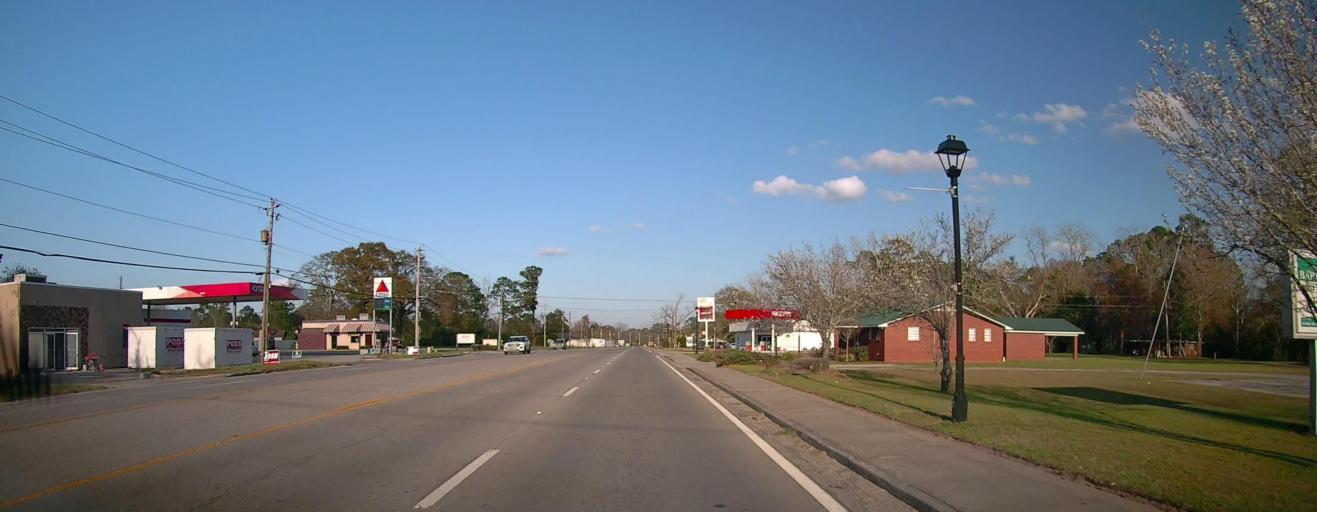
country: US
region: Georgia
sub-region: Evans County
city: Claxton
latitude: 32.1585
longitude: -81.9344
